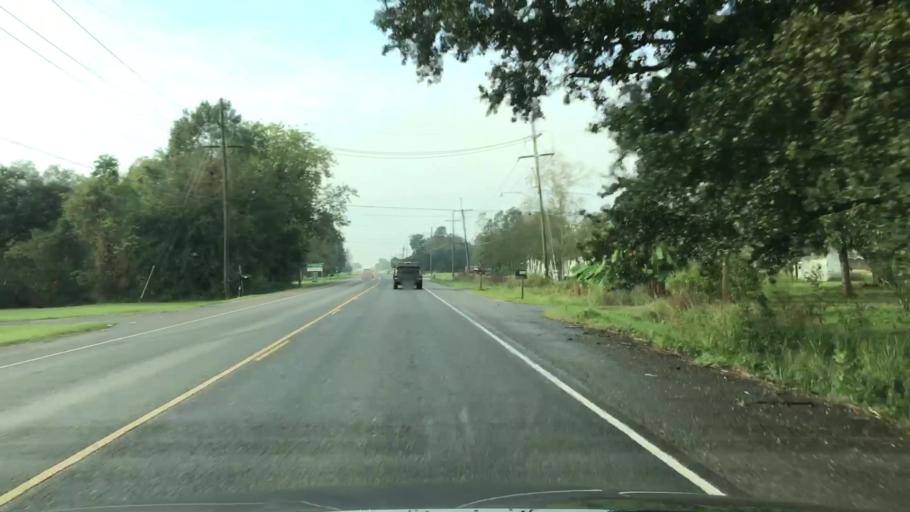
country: US
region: Louisiana
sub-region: Terrebonne Parish
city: Gray
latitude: 29.6734
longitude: -90.8152
